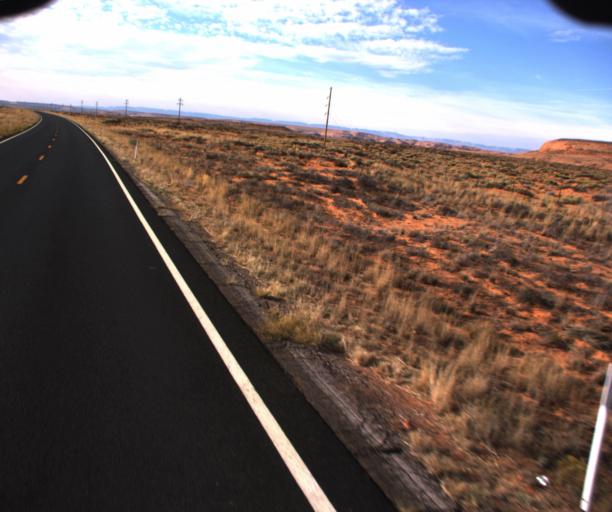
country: US
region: Arizona
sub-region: Apache County
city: Many Farms
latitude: 36.8390
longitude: -109.6421
